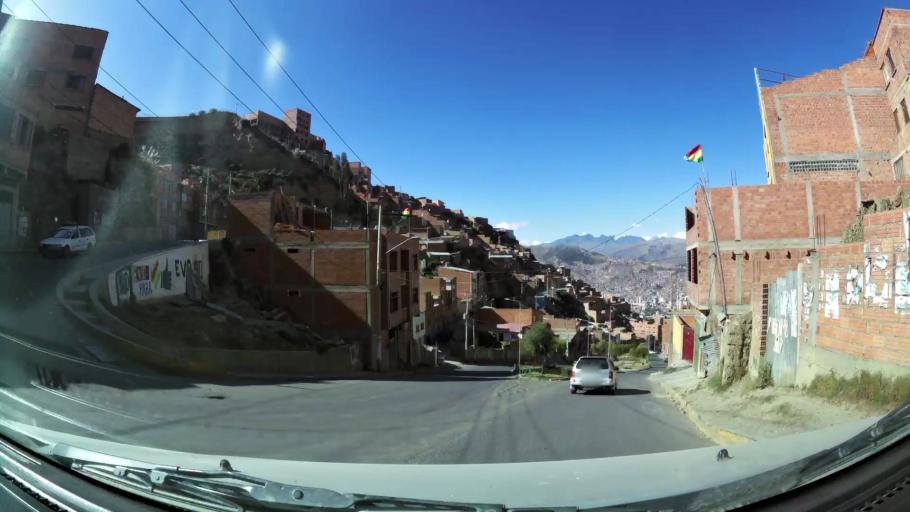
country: BO
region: La Paz
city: La Paz
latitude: -16.5110
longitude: -68.1495
